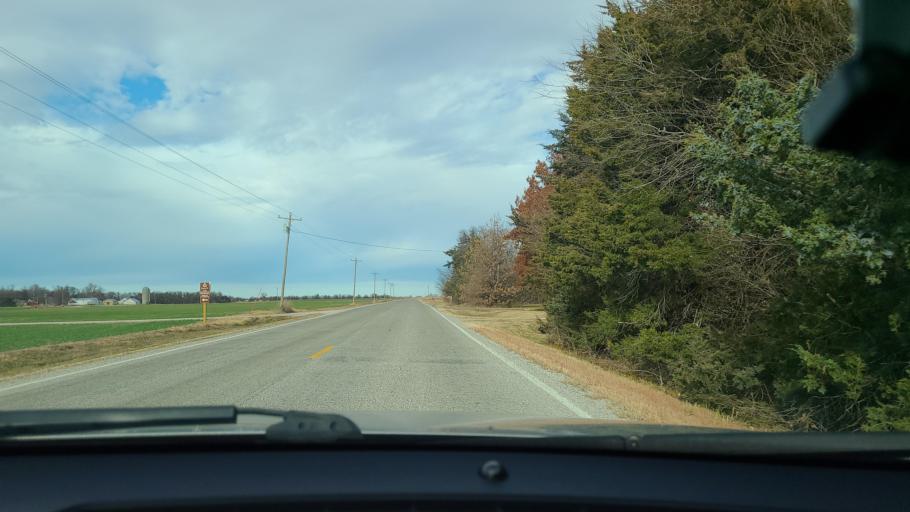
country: US
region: Kansas
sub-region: McPherson County
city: Inman
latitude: 38.3144
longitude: -97.9248
